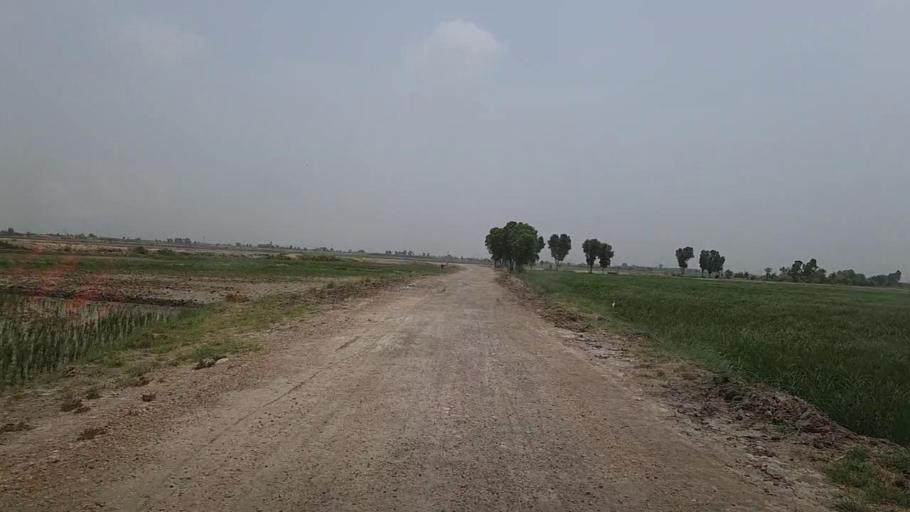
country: PK
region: Sindh
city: Sita Road
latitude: 27.0674
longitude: 67.8599
